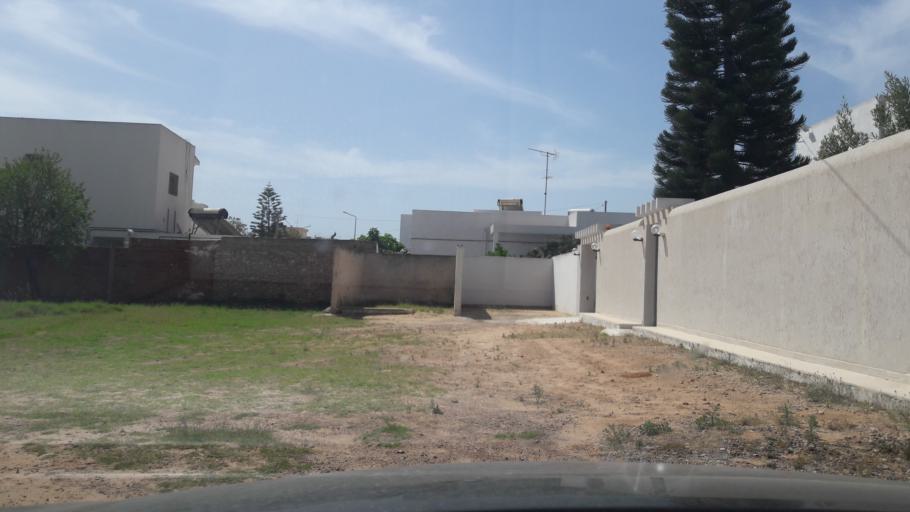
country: TN
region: Safaqis
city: Al Qarmadah
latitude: 34.7904
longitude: 10.7553
